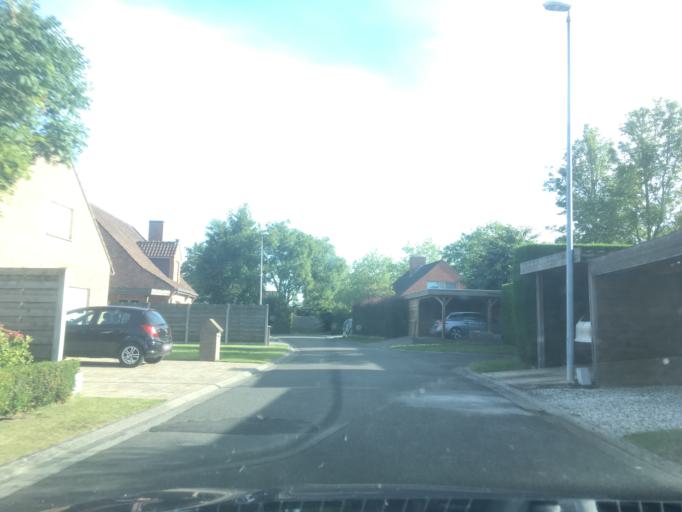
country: BE
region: Flanders
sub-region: Provincie West-Vlaanderen
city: Izegem
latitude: 50.9227
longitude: 3.1836
